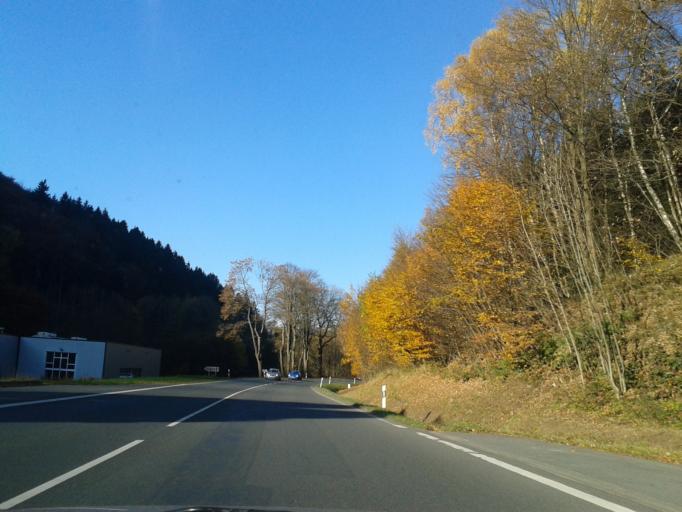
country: DE
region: North Rhine-Westphalia
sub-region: Regierungsbezirk Arnsberg
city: Olsberg
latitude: 51.3349
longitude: 8.4880
